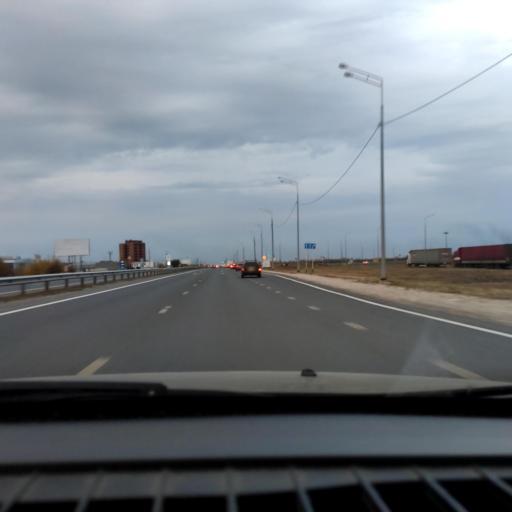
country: RU
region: Samara
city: Tol'yatti
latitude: 53.5524
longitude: 49.3370
